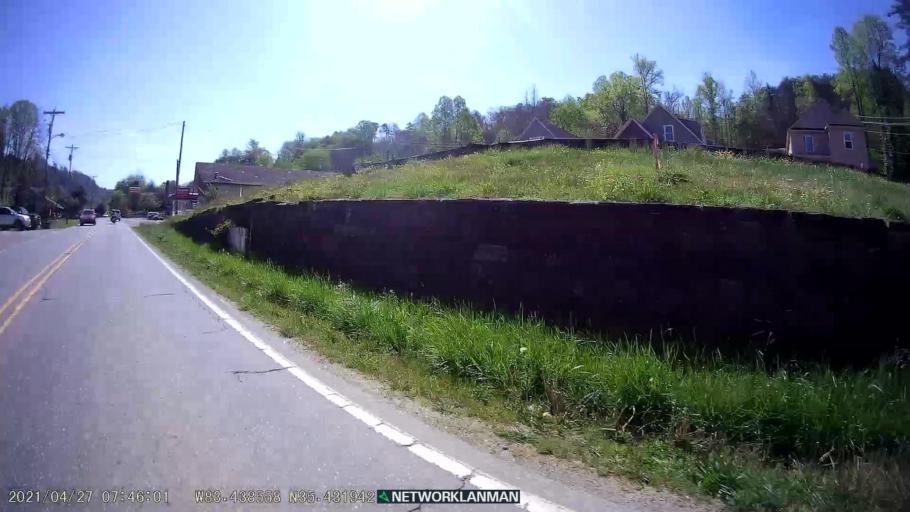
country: US
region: North Carolina
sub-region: Swain County
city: Bryson City
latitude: 35.4319
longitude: -83.4384
